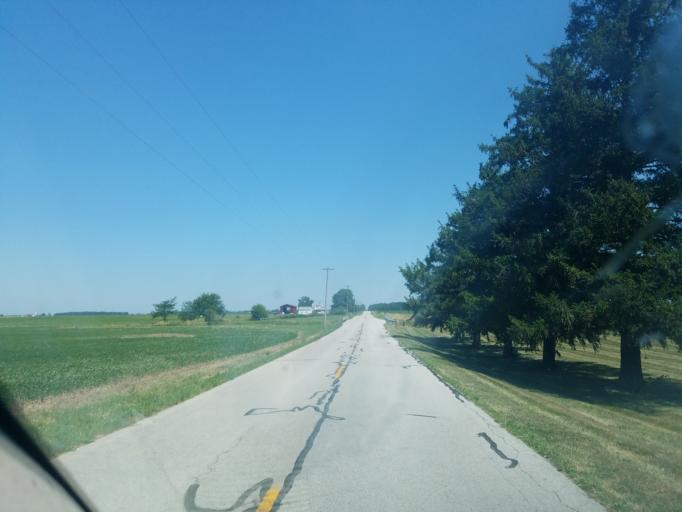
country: US
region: Ohio
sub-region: Mercer County
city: Rockford
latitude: 40.6607
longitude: -84.7086
